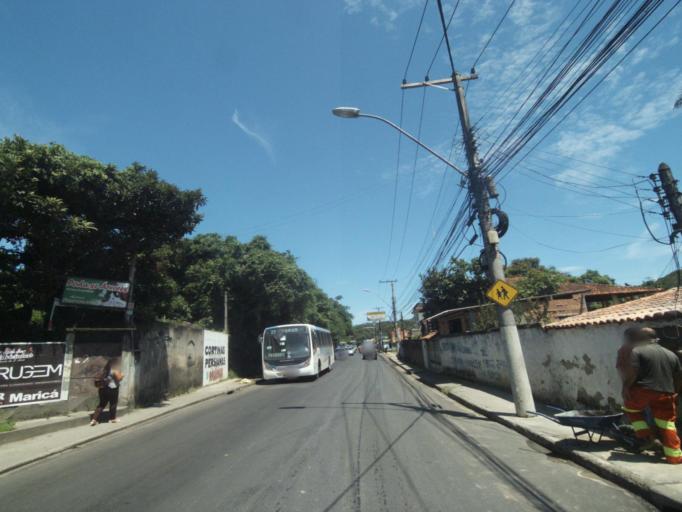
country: BR
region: Rio de Janeiro
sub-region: Sao Goncalo
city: Sao Goncalo
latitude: -22.9087
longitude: -42.9845
